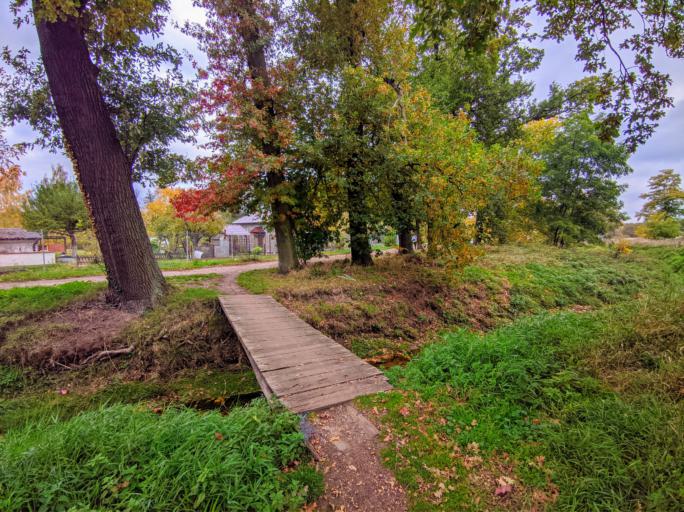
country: PL
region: Lubusz
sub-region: Powiat zarski
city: Lubsko
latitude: 51.7890
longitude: 14.9651
